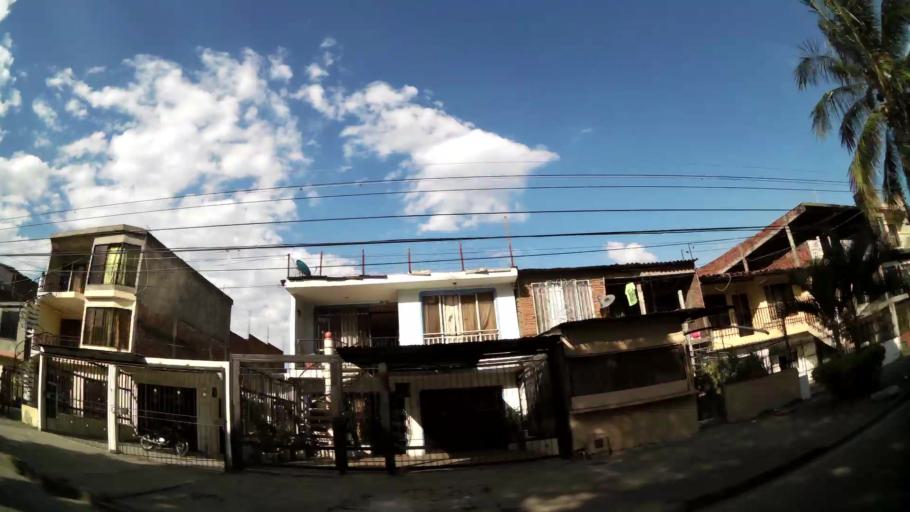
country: CO
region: Valle del Cauca
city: Cali
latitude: 3.4073
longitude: -76.5098
